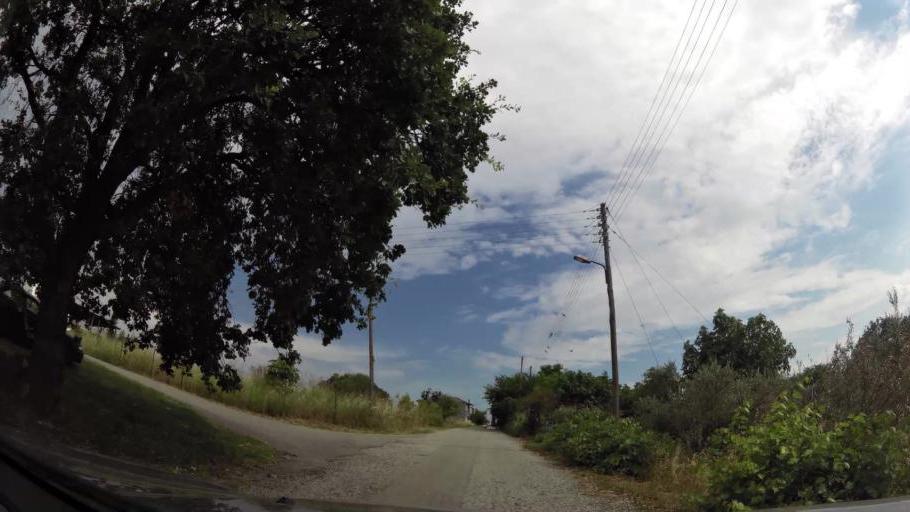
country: GR
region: Central Macedonia
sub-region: Nomos Pierias
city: Makrygialos
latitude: 40.4209
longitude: 22.6066
